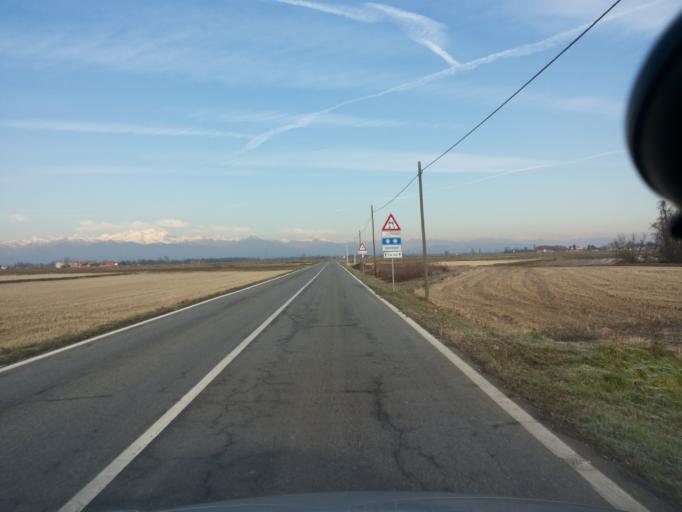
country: IT
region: Piedmont
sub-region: Provincia di Vercelli
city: Oldenico
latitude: 45.4048
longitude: 8.3784
